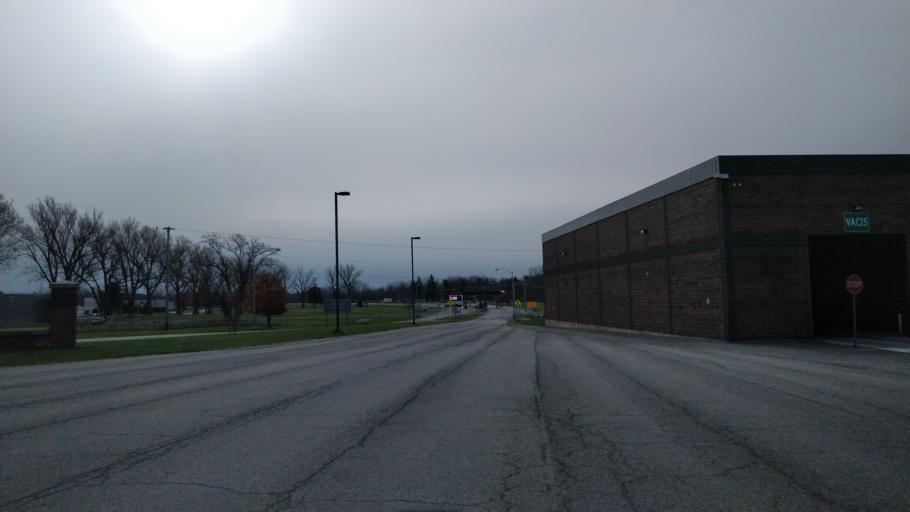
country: US
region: New York
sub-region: St. Lawrence County
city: Ogdensburg
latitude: 44.7209
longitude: -75.4545
